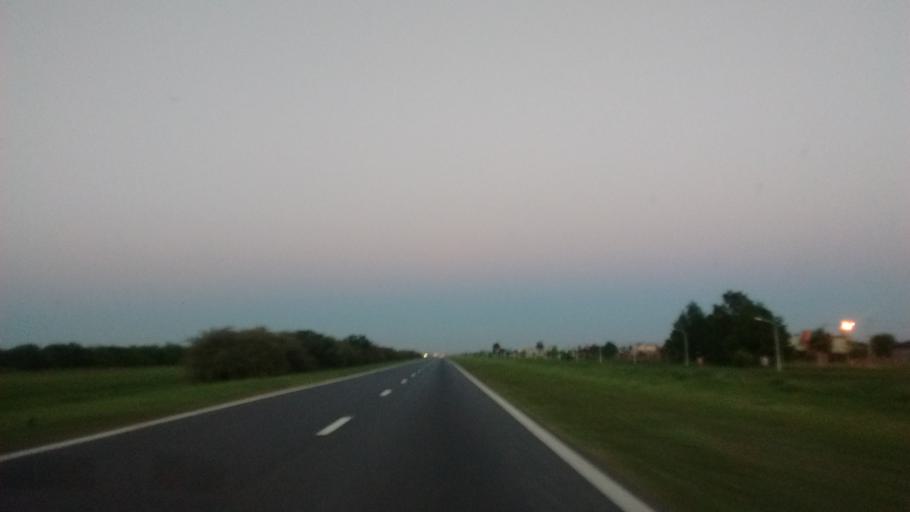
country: AR
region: Santa Fe
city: Roldan
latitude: -32.9186
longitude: -60.9322
